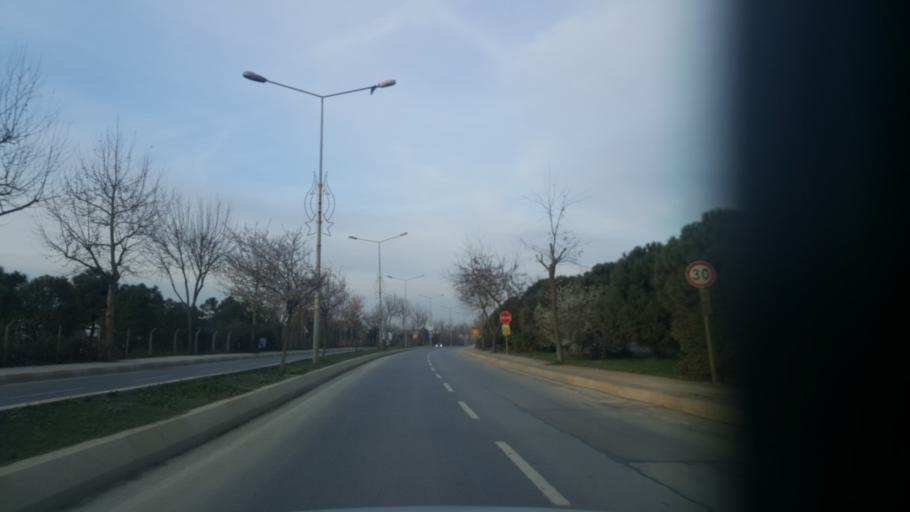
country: TR
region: Istanbul
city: Icmeler
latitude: 40.8276
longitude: 29.2925
